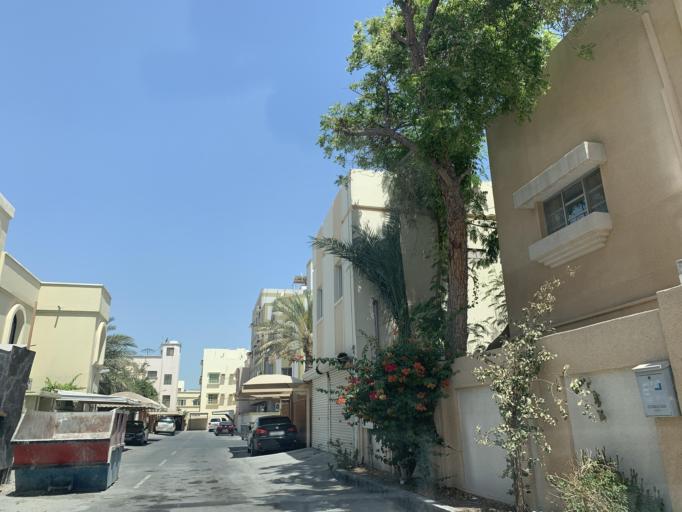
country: BH
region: Northern
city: Ar Rifa'
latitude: 26.1337
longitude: 50.5782
